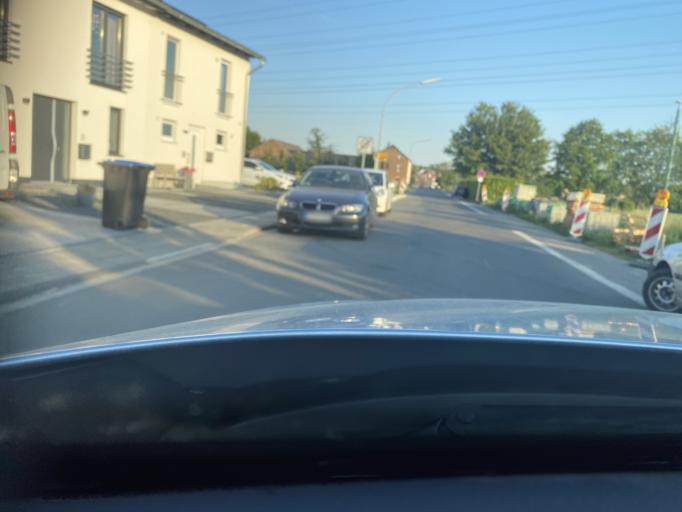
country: DE
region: North Rhine-Westphalia
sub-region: Regierungsbezirk Dusseldorf
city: Grevenbroich
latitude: 51.1091
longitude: 6.5460
